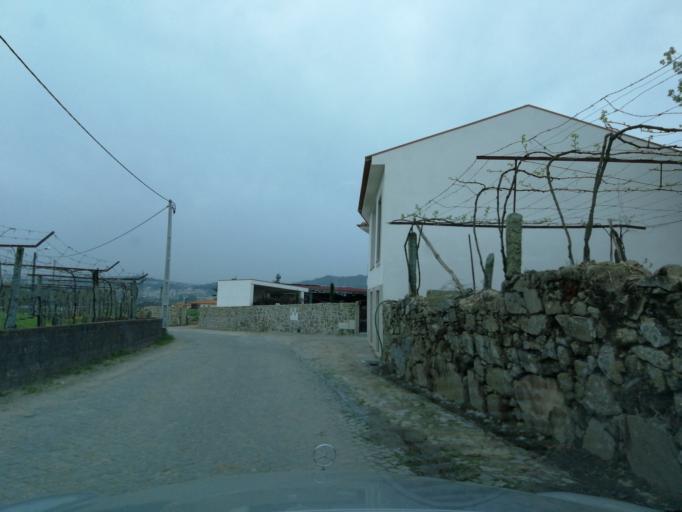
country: PT
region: Braga
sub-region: Braga
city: Braga
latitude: 41.5787
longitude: -8.4396
